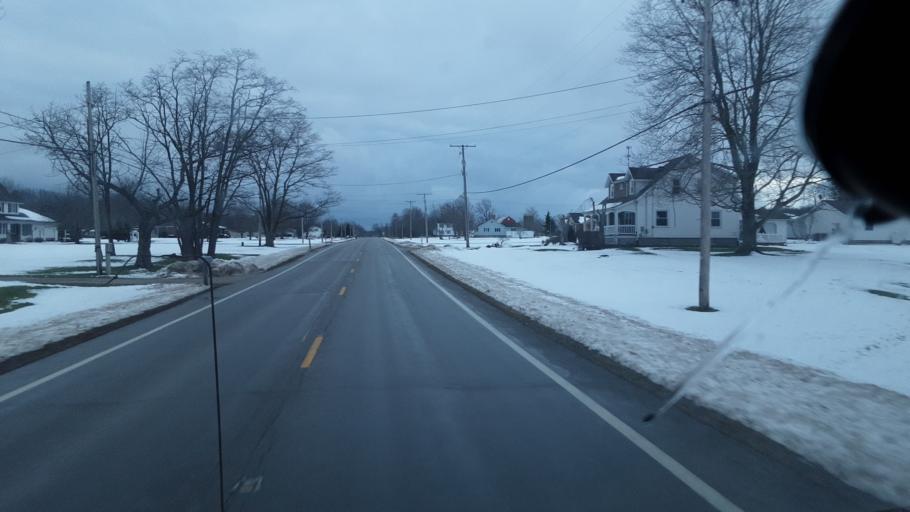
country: US
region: Ohio
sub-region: Ashtabula County
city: Jefferson
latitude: 41.7255
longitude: -80.7542
